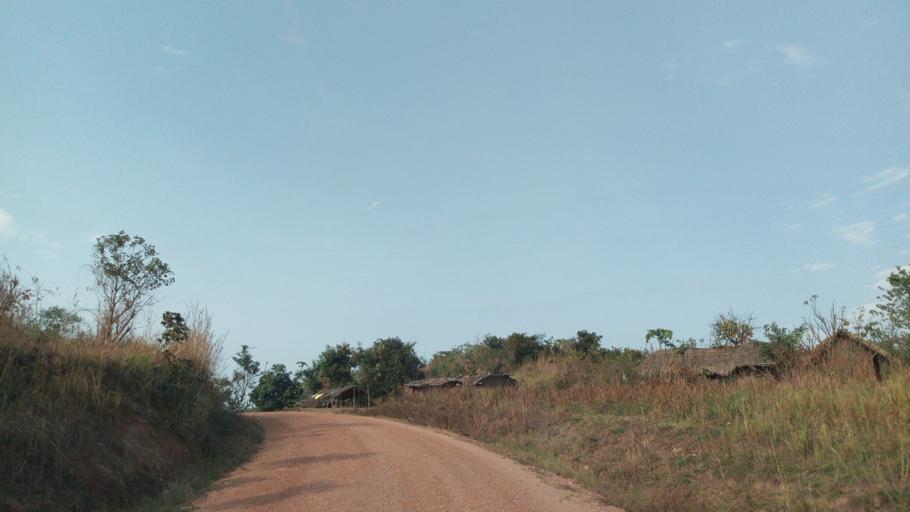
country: CD
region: Katanga
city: Kalemie
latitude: -6.0031
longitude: 29.0547
